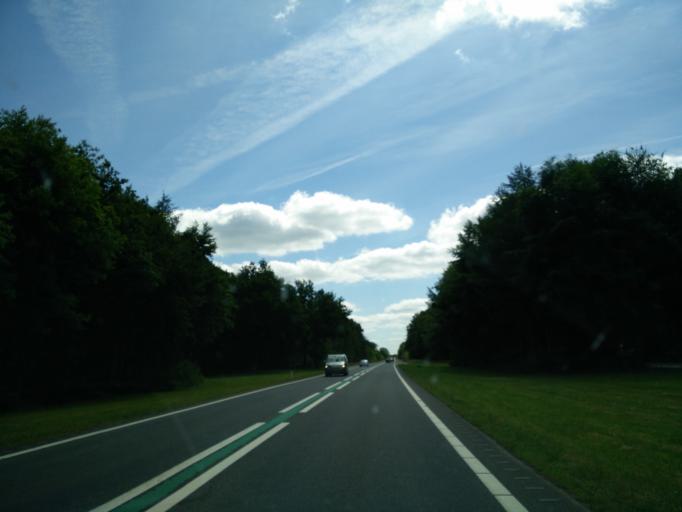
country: NL
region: Drenthe
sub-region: Gemeente Coevorden
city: Sleen
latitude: 52.8144
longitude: 6.6775
